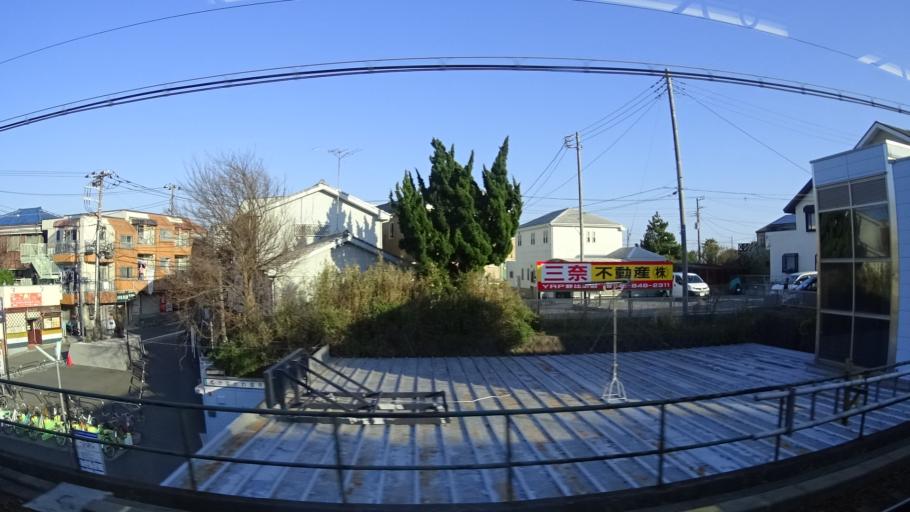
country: JP
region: Kanagawa
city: Miura
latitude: 35.1987
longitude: 139.6655
